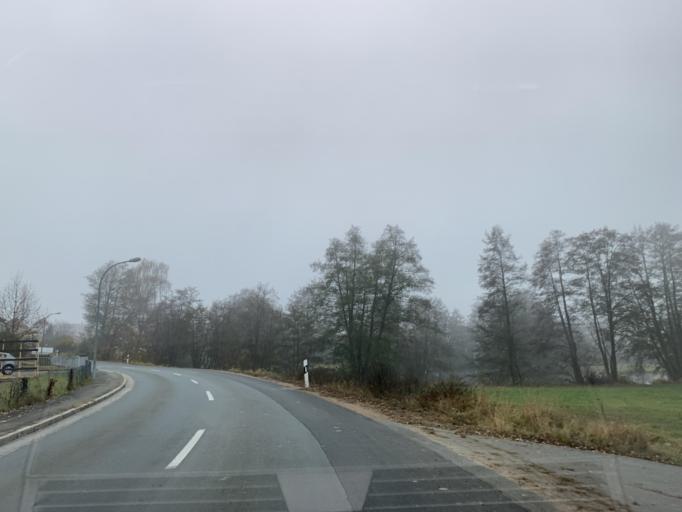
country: DE
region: Bavaria
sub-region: Upper Palatinate
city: Neunburg vorm Wald
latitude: 49.3533
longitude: 12.3901
